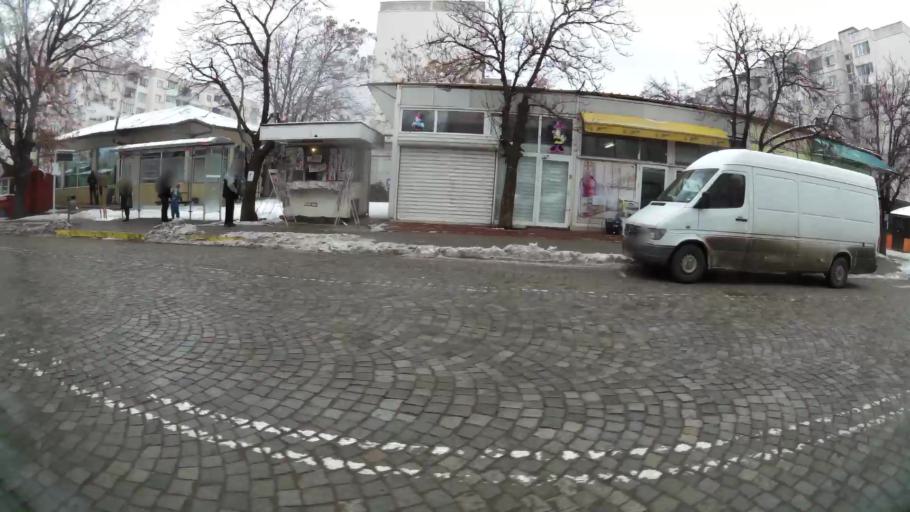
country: BG
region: Sofia-Capital
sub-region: Stolichna Obshtina
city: Sofia
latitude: 42.7138
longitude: 23.2985
